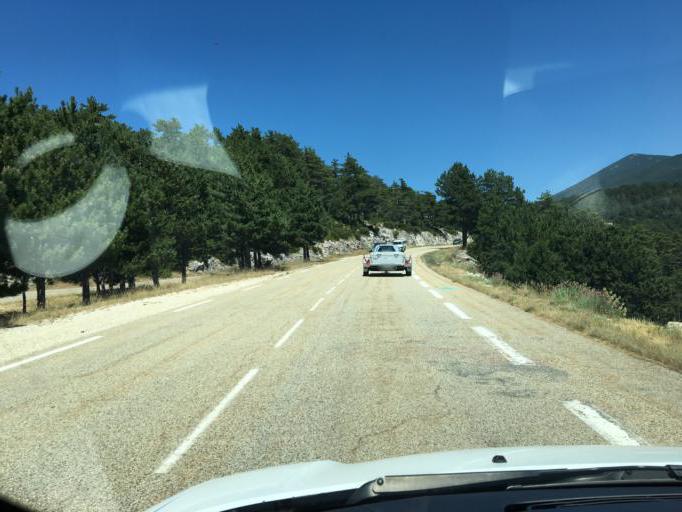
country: FR
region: Provence-Alpes-Cote d'Azur
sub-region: Departement du Vaucluse
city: Bedoin
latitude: 44.1674
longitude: 5.1821
